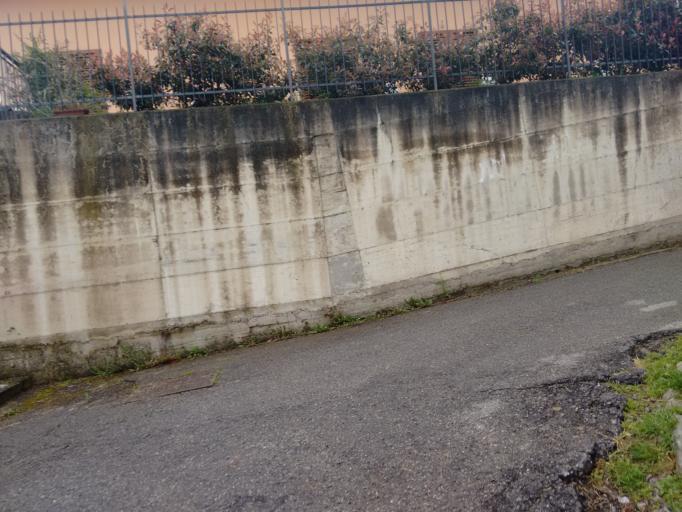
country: IT
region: Tuscany
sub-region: Province of Florence
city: Strada in Chianti
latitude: 43.6569
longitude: 11.3016
